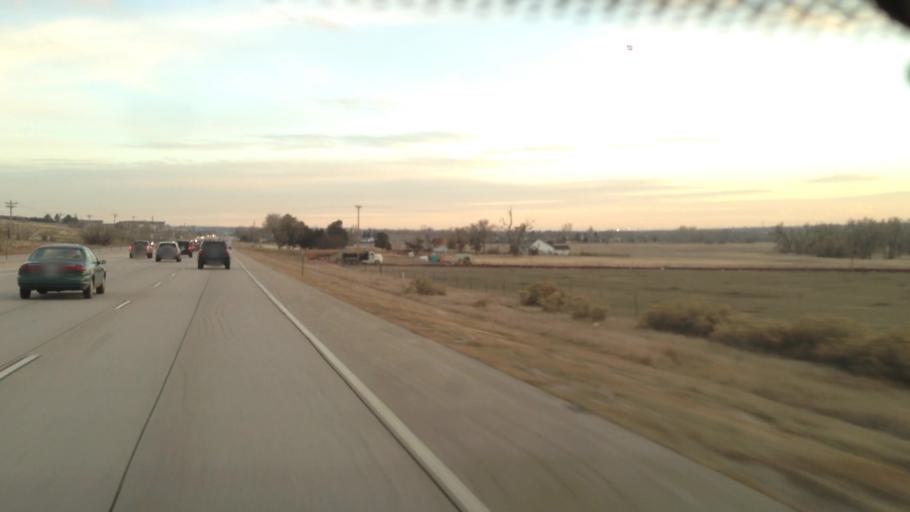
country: US
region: Colorado
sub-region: Arapahoe County
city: Dove Valley
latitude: 39.5712
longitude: -104.7888
